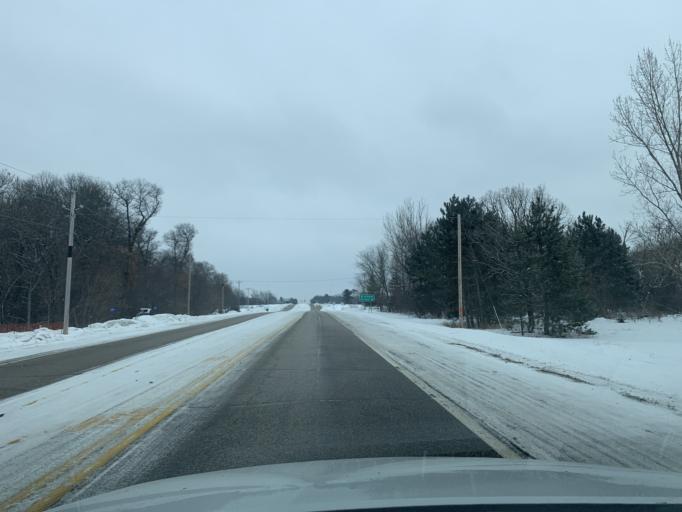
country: US
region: Minnesota
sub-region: Sherburne County
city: Zimmerman
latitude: 45.5016
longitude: -93.5886
